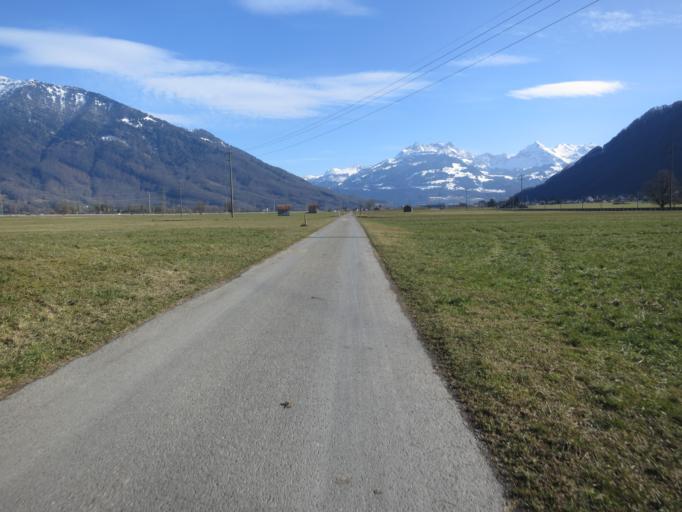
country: CH
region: Glarus
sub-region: Glarus
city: Bilten
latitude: 47.1629
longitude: 9.0109
